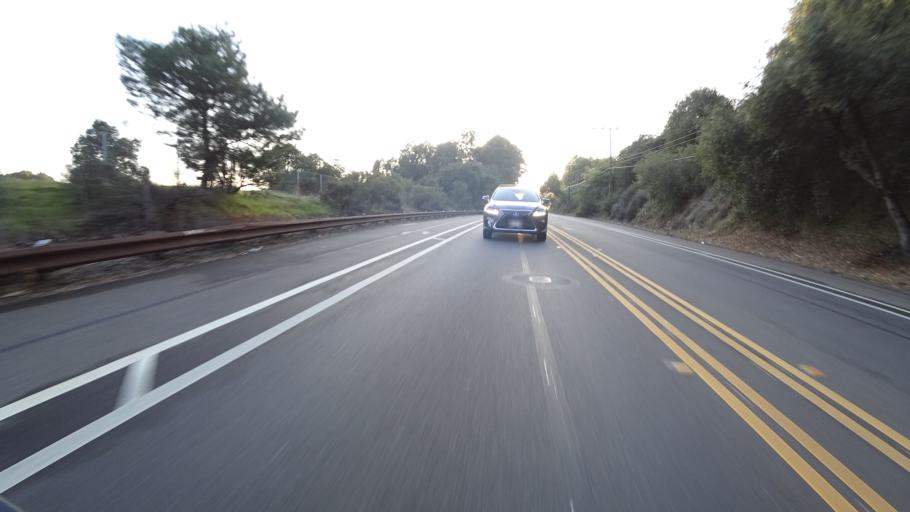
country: US
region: California
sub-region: Alameda County
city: Fairview
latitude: 37.6988
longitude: -122.0430
